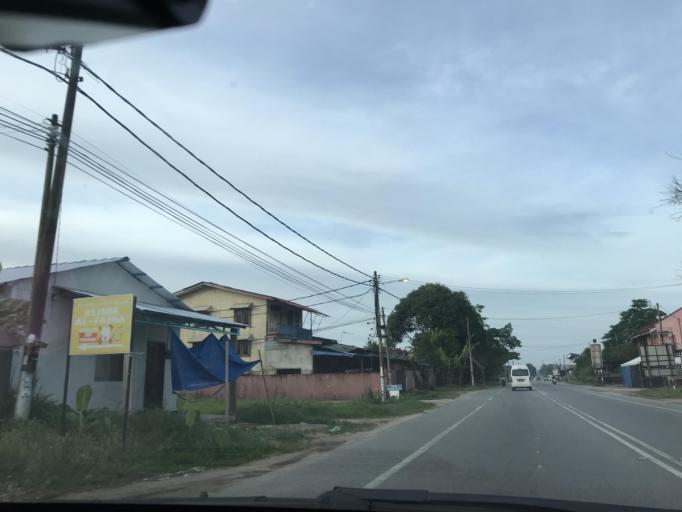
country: MY
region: Kelantan
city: Kota Bharu
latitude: 6.1088
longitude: 102.2127
